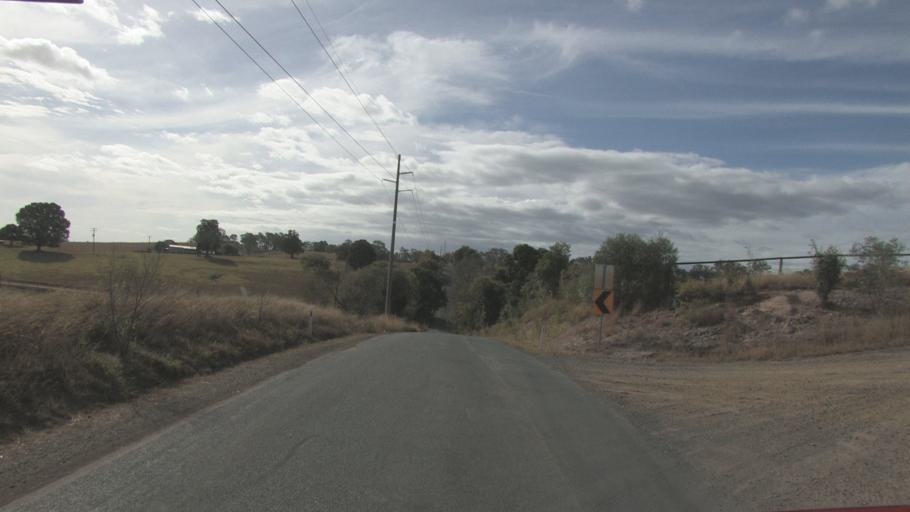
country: AU
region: Queensland
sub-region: Logan
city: Cedar Vale
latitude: -27.9045
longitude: 153.0145
